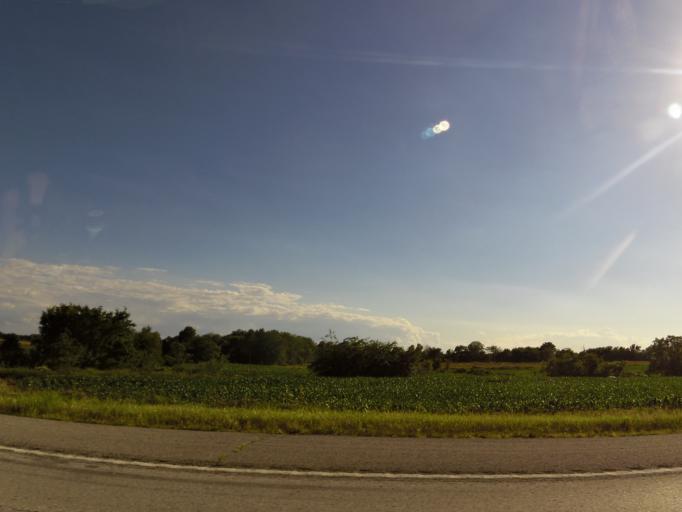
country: US
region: Missouri
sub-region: Pike County
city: Bowling Green
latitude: 39.2795
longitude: -91.0973
